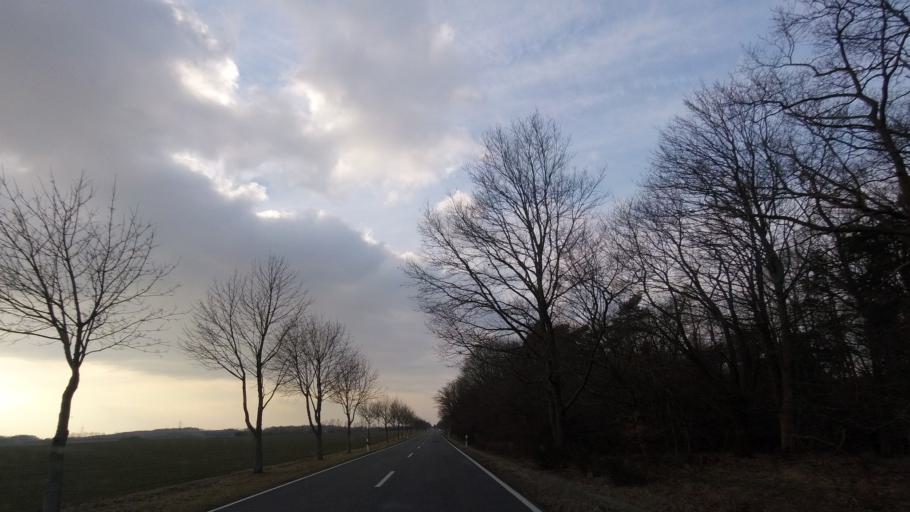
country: DE
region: Brandenburg
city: Belzig
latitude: 52.1526
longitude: 12.5527
